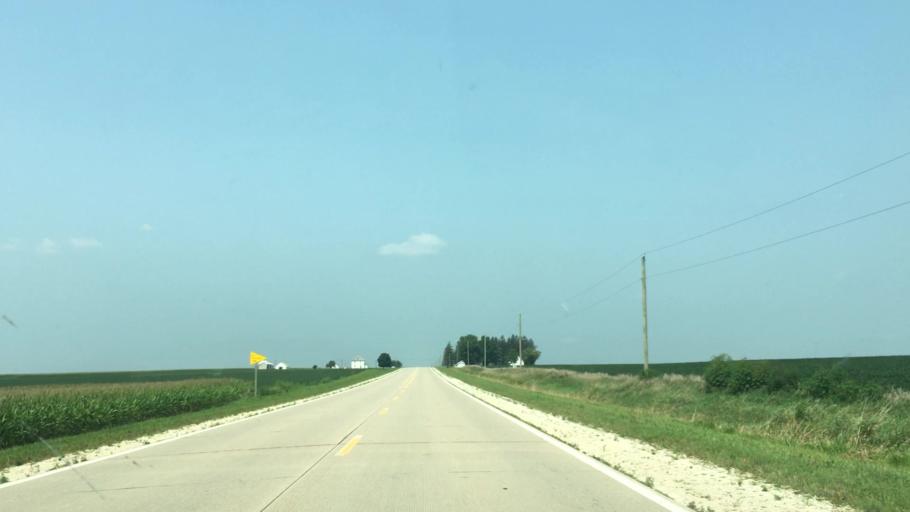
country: US
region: Iowa
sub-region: Fayette County
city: Oelwein
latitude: 42.7058
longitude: -91.8048
